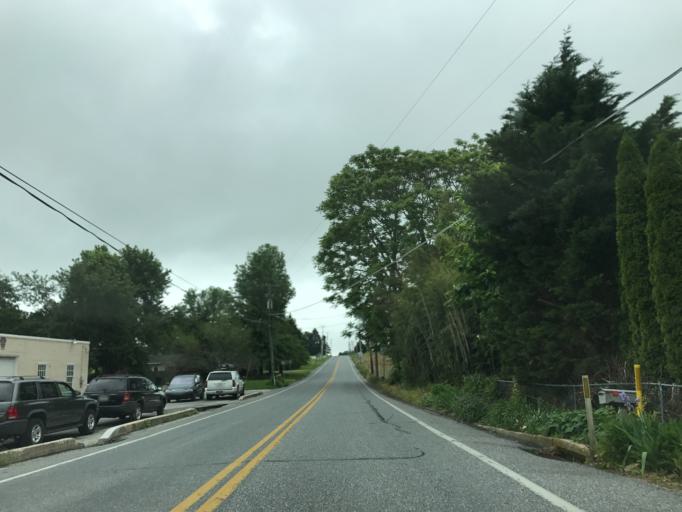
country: US
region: Pennsylvania
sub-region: York County
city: Stewartstown
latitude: 39.8252
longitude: -76.6115
